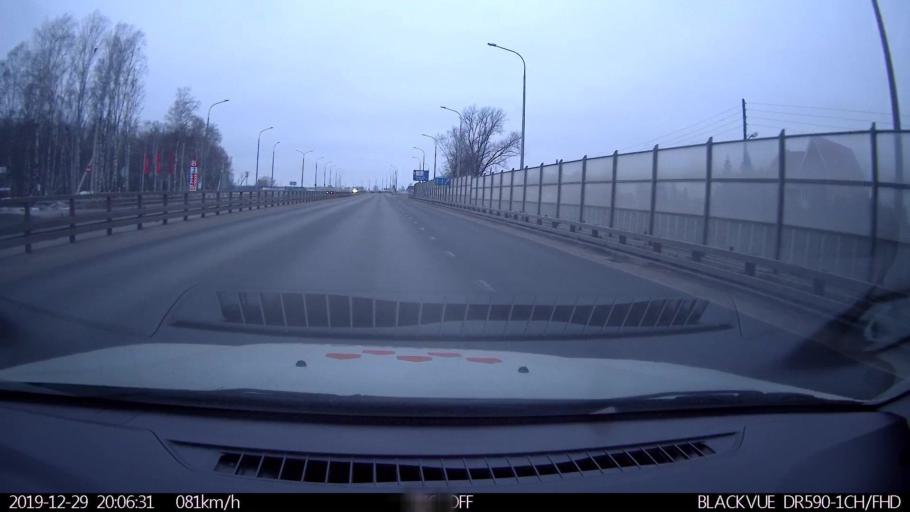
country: RU
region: Nizjnij Novgorod
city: Neklyudovo
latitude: 56.3962
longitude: 44.0011
